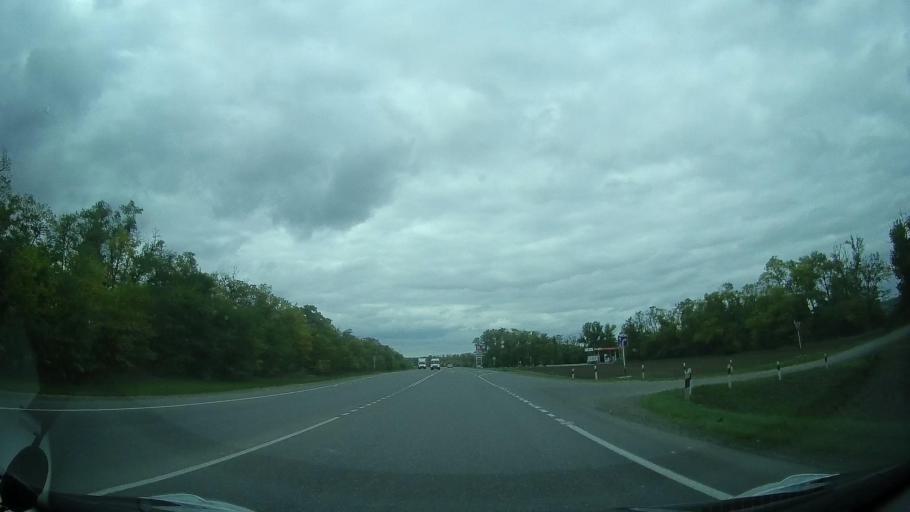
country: RU
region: Rostov
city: Mechetinskaya
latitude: 46.7521
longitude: 40.4604
